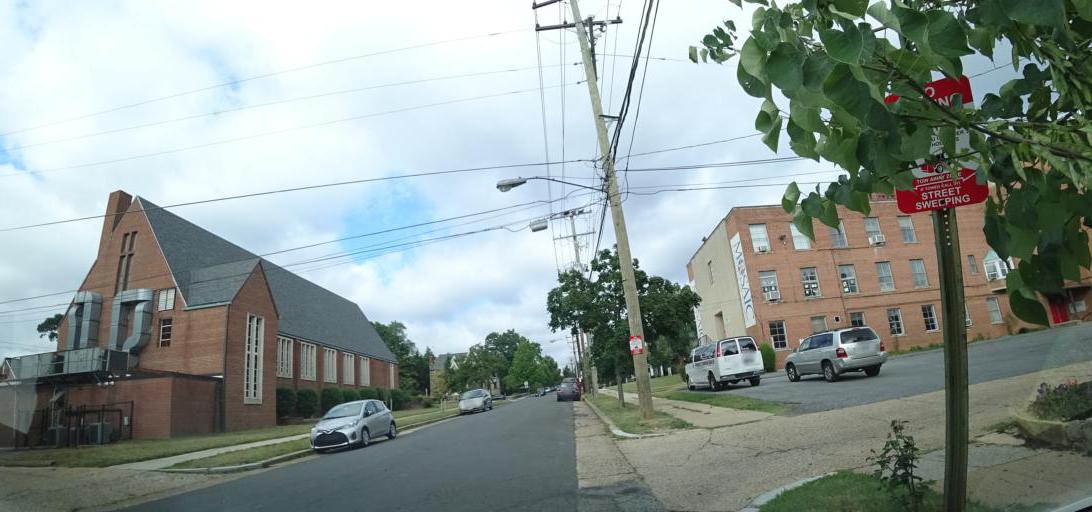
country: US
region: Maryland
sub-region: Montgomery County
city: Takoma Park
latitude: 38.9441
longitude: -77.0354
